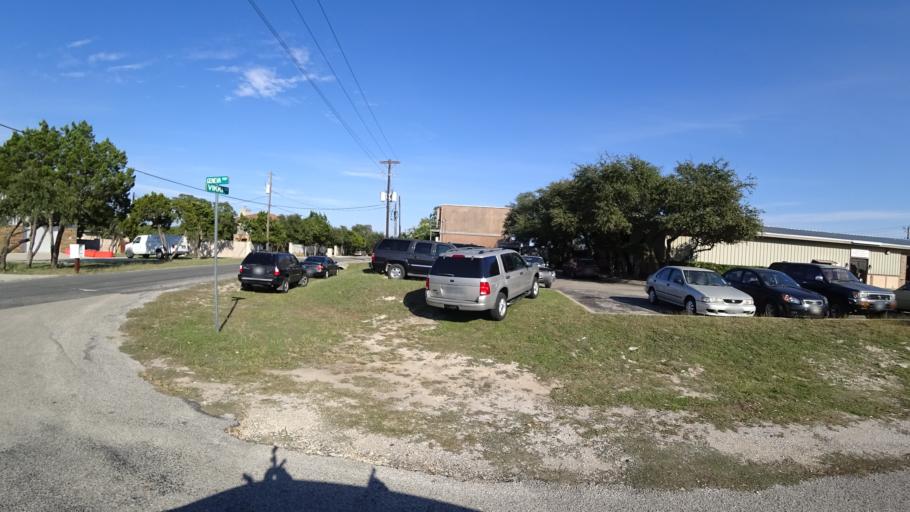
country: US
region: Texas
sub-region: Travis County
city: Bee Cave
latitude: 30.2318
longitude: -97.9319
